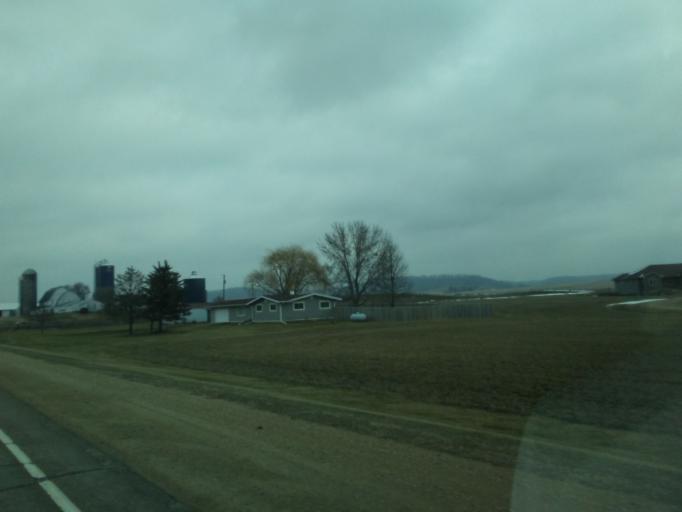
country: US
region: Wisconsin
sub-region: Richland County
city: Richland Center
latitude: 43.2269
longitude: -90.2914
